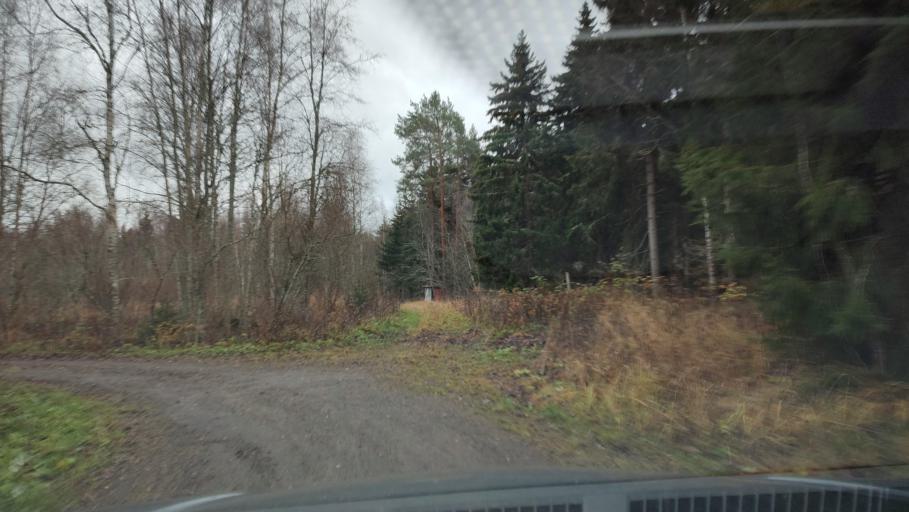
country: FI
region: Ostrobothnia
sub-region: Sydosterbotten
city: Kristinestad
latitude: 62.2769
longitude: 21.4136
